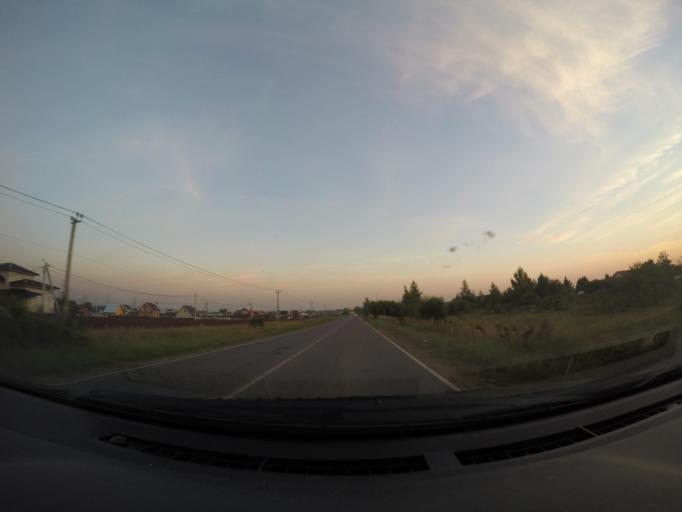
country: RU
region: Moskovskaya
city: Rechitsy
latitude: 55.5997
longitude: 38.5250
